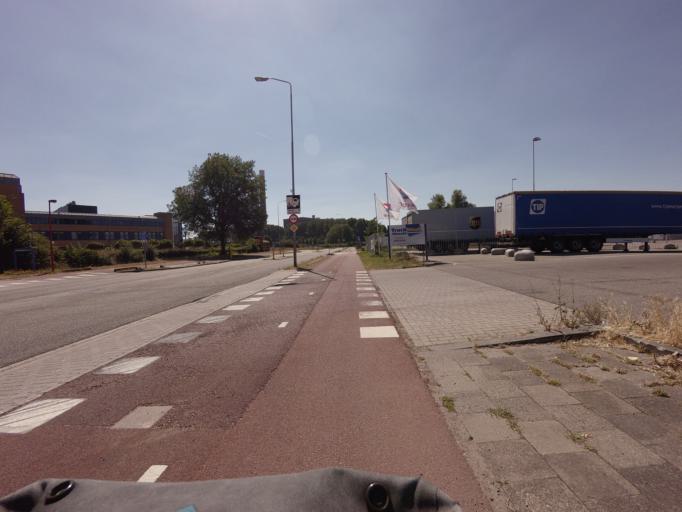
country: NL
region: Utrecht
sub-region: Stichtse Vecht
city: Maarssen
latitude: 52.1066
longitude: 5.0663
